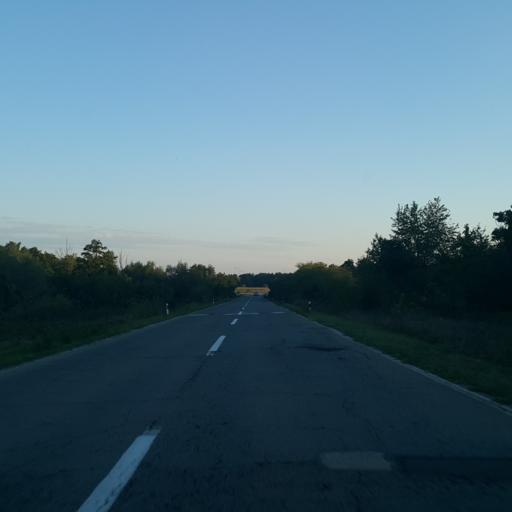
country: RS
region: Central Serbia
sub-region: Borski Okrug
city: Negotin
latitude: 44.1817
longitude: 22.3655
